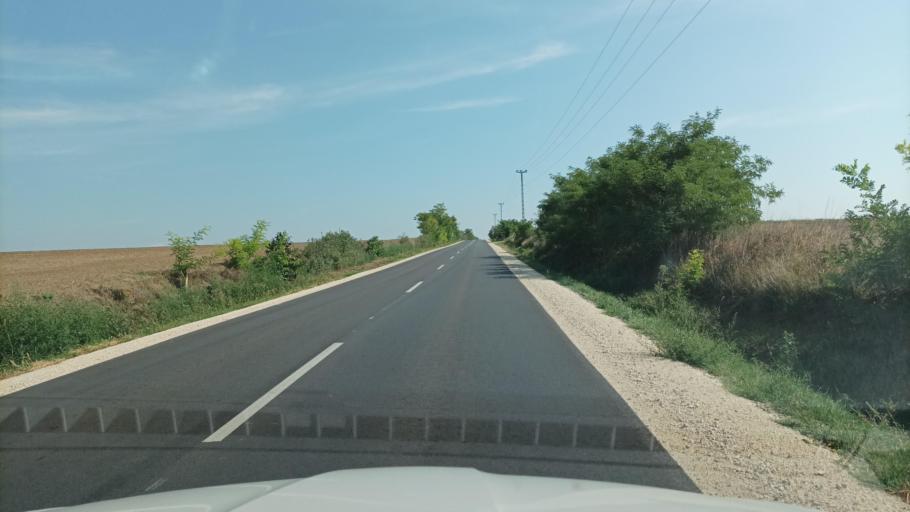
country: HU
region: Pest
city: Vacszentlaszlo
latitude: 47.5774
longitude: 19.5484
